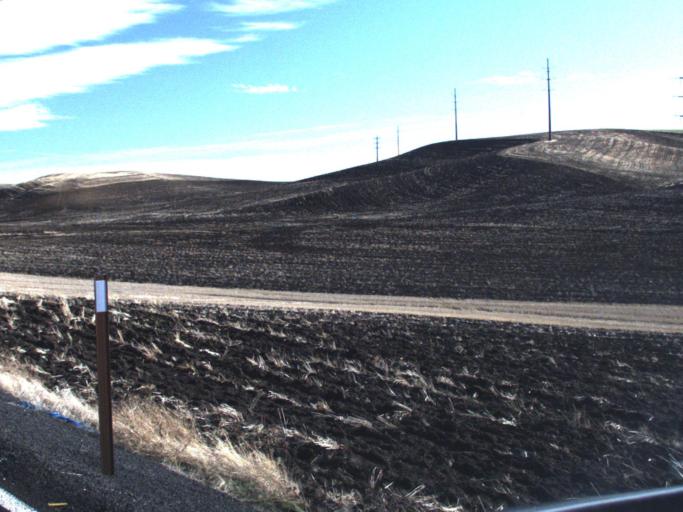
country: US
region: Washington
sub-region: Whitman County
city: Colfax
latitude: 46.8893
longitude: -117.3422
